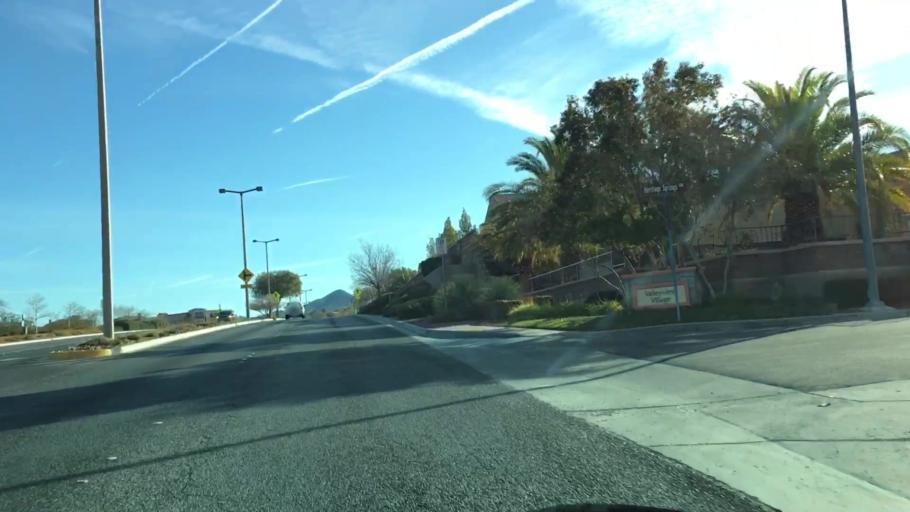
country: US
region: Nevada
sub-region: Clark County
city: Whitney
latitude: 35.9693
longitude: -115.1108
